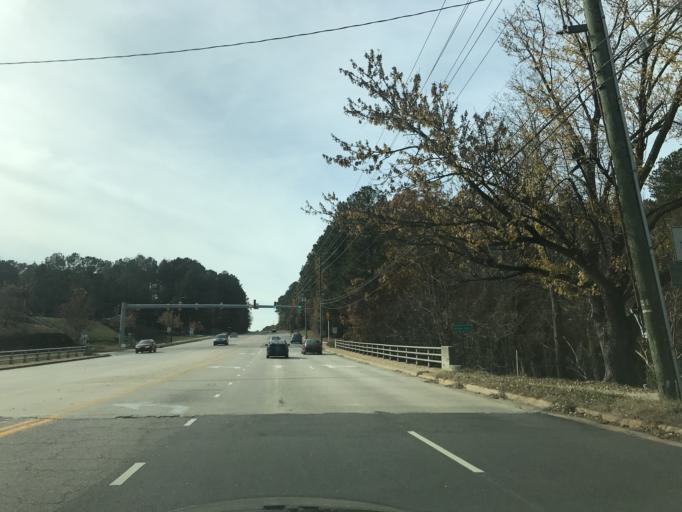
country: US
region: North Carolina
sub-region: Wake County
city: West Raleigh
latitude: 35.8418
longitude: -78.6835
